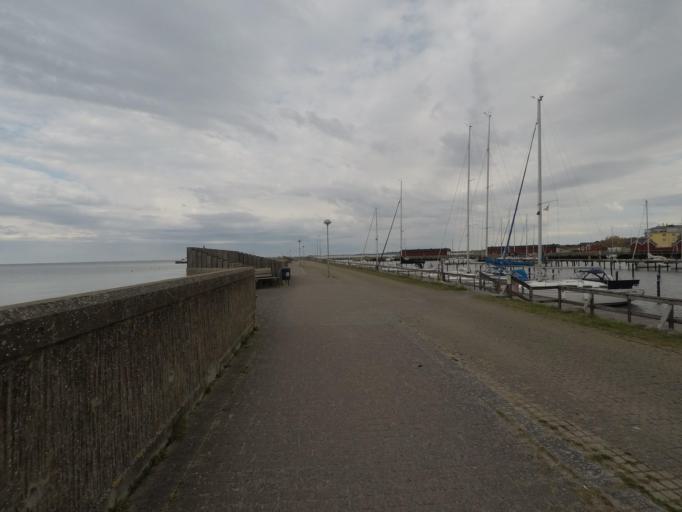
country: SE
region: Skane
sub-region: Lomma Kommun
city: Lomma
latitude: 55.6738
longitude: 13.0589
